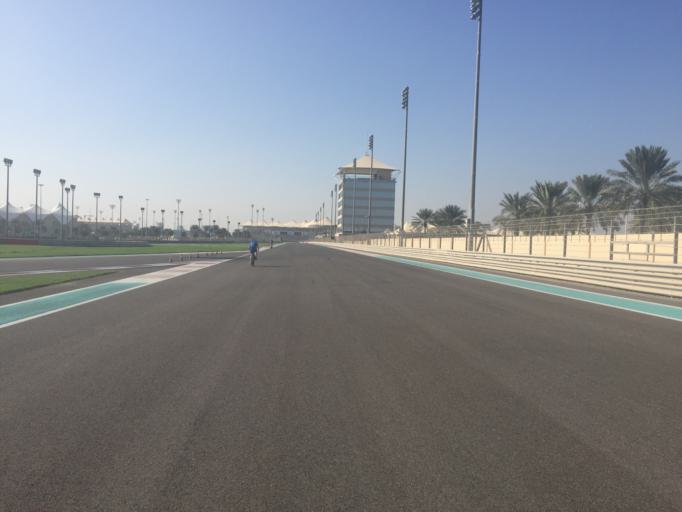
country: AE
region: Abu Dhabi
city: Abu Dhabi
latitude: 24.4752
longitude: 54.6039
